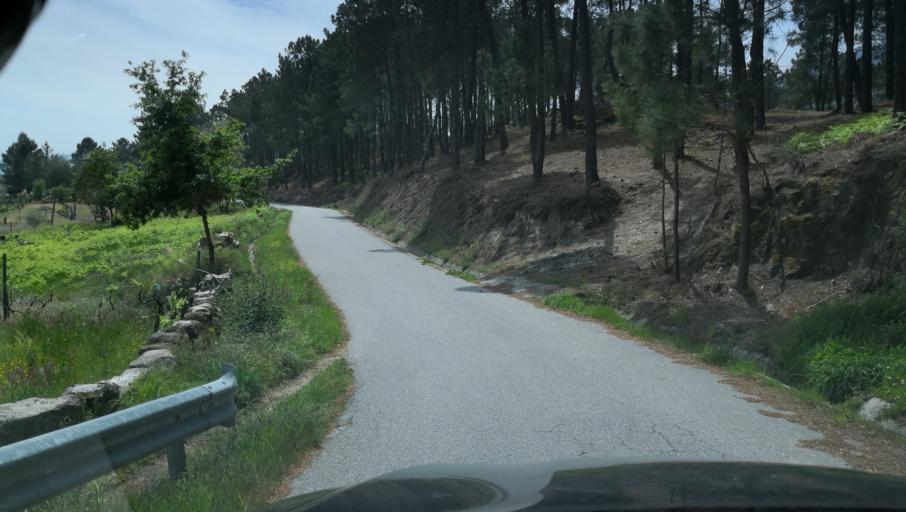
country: PT
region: Vila Real
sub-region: Vila Real
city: Vila Real
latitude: 41.3172
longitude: -7.7889
